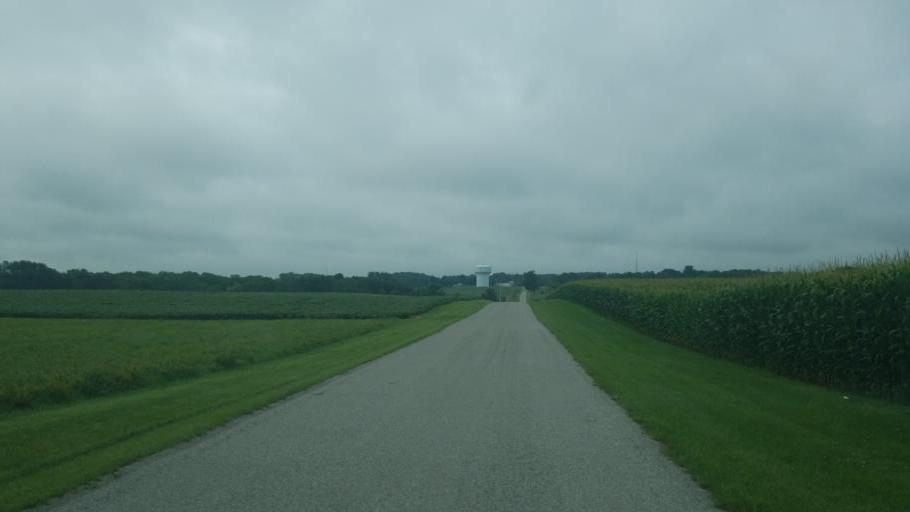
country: US
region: Ohio
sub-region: Knox County
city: Centerburg
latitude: 40.4156
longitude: -82.6812
